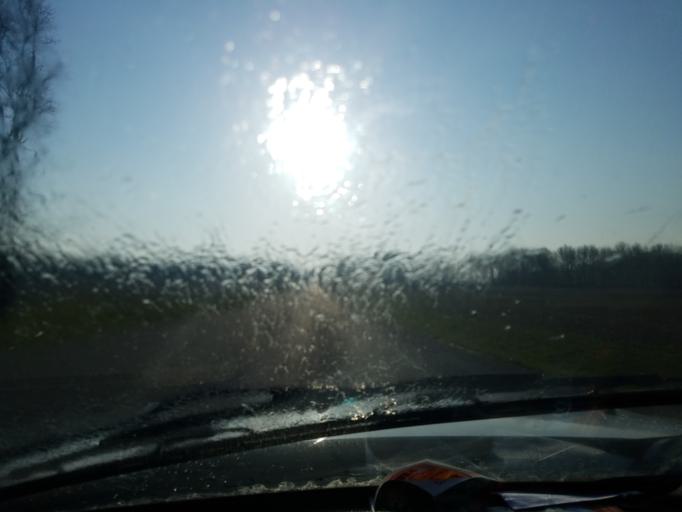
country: US
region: Indiana
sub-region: Vigo County
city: Seelyville
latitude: 39.3896
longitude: -87.2208
